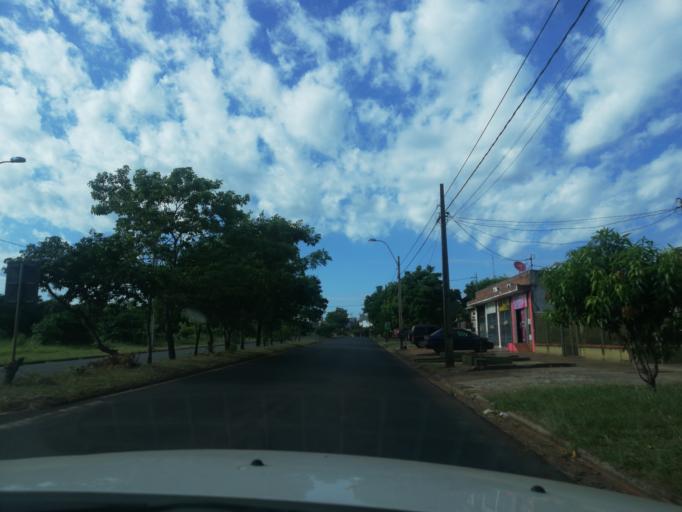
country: PY
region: Itapua
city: Encarnacion
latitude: -27.3516
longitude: -55.8491
